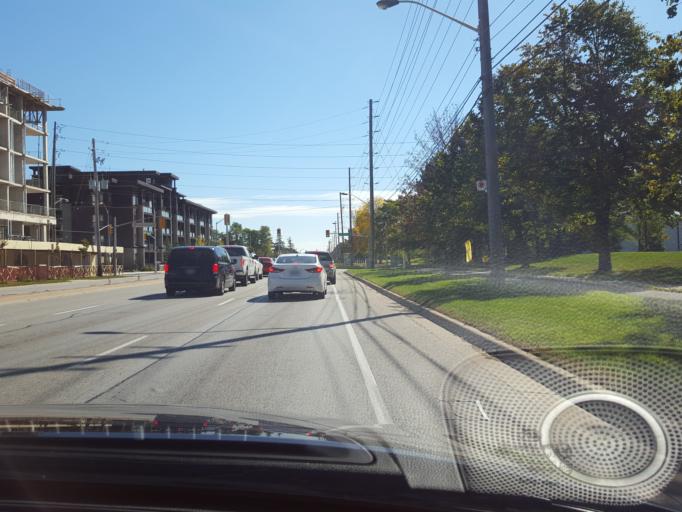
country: CA
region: Ontario
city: Burlington
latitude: 43.3910
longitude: -79.7865
